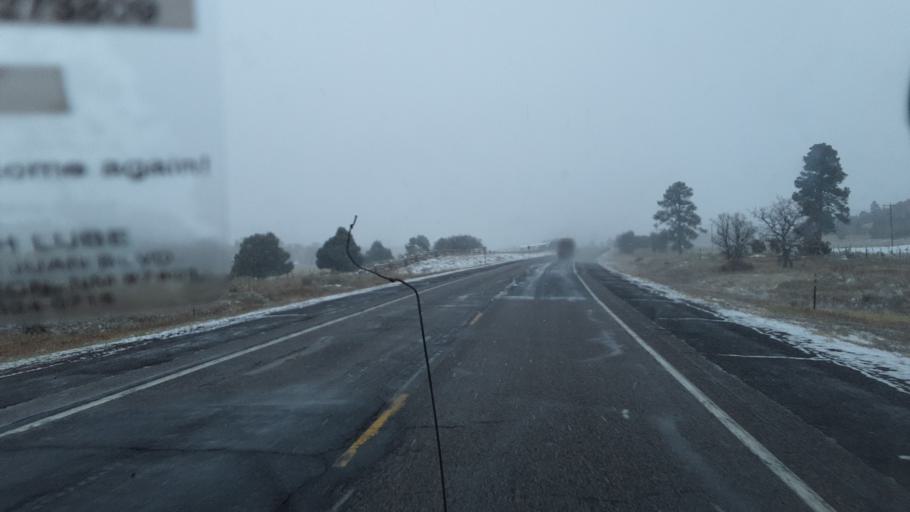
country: US
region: New Mexico
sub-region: Rio Arriba County
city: Chama
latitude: 36.8229
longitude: -106.5693
